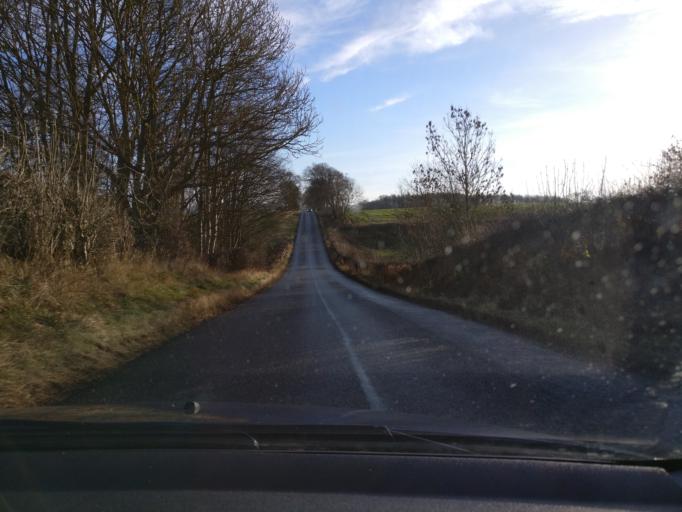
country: GB
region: Scotland
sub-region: The Scottish Borders
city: Kelso
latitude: 55.5291
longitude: -2.4309
